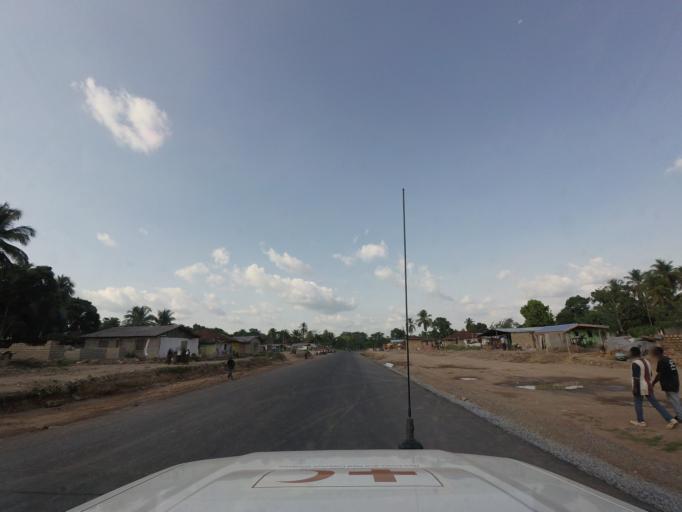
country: LR
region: Bong
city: Gbarnga
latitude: 7.0096
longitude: -9.5652
